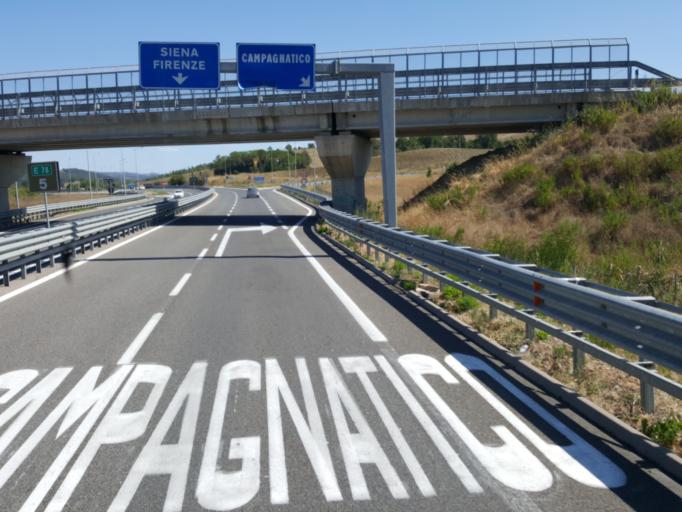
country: IT
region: Tuscany
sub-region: Provincia di Grosseto
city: Campagnatico
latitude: 42.8897
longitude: 11.2357
